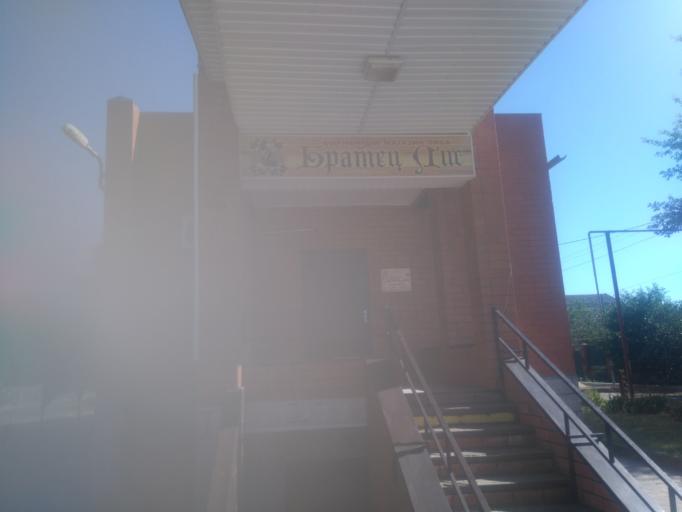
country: RU
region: Krasnodarskiy
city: Fastovetskaya
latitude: 45.9066
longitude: 40.1505
